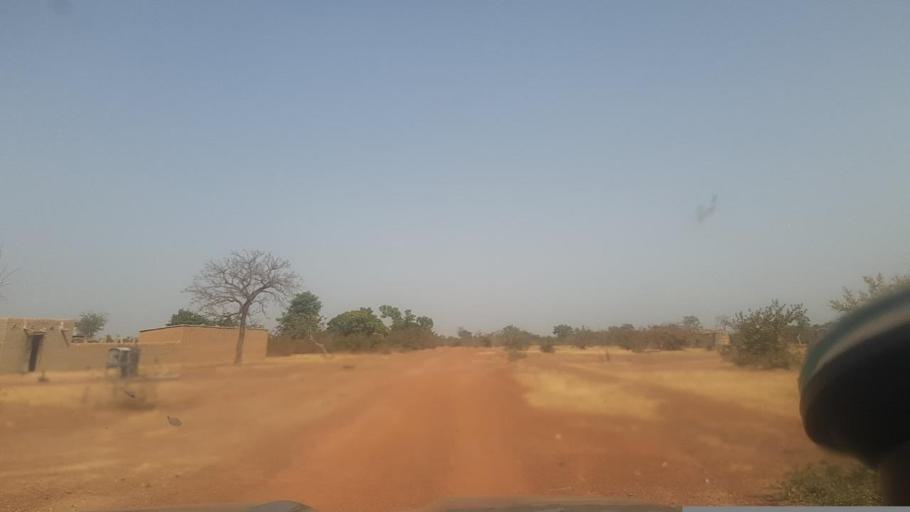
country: ML
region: Segou
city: Bla
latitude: 12.8573
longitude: -5.9718
